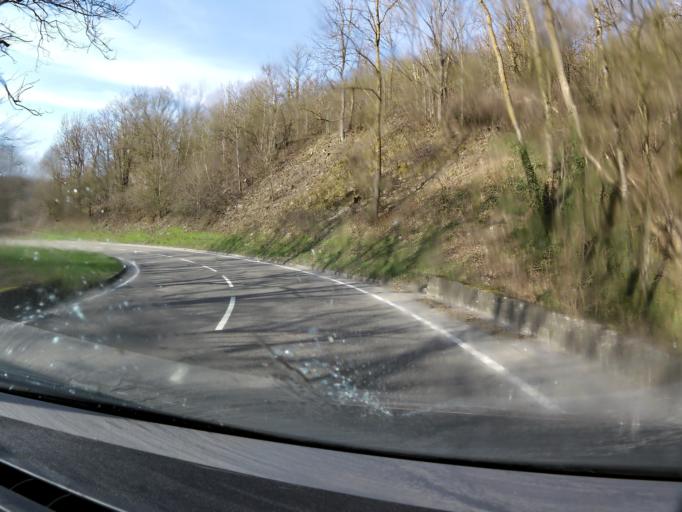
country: DE
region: Bavaria
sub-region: Regierungsbezirk Mittelfranken
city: Rothenburg ob der Tauber
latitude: 49.3868
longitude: 10.1722
